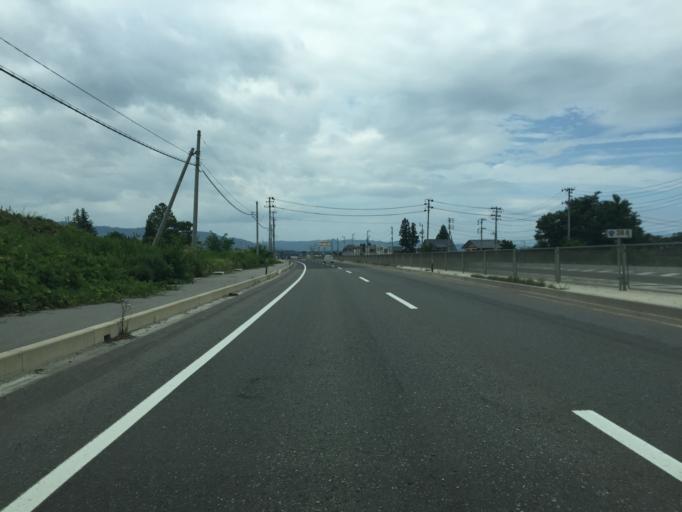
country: JP
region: Yamagata
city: Yonezawa
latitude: 37.8952
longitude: 140.1608
